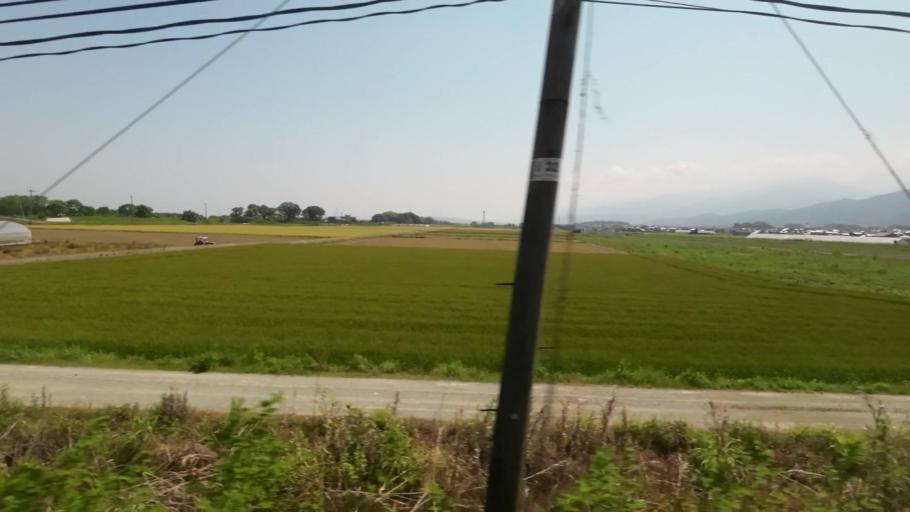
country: JP
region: Ehime
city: Saijo
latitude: 33.9025
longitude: 133.0996
